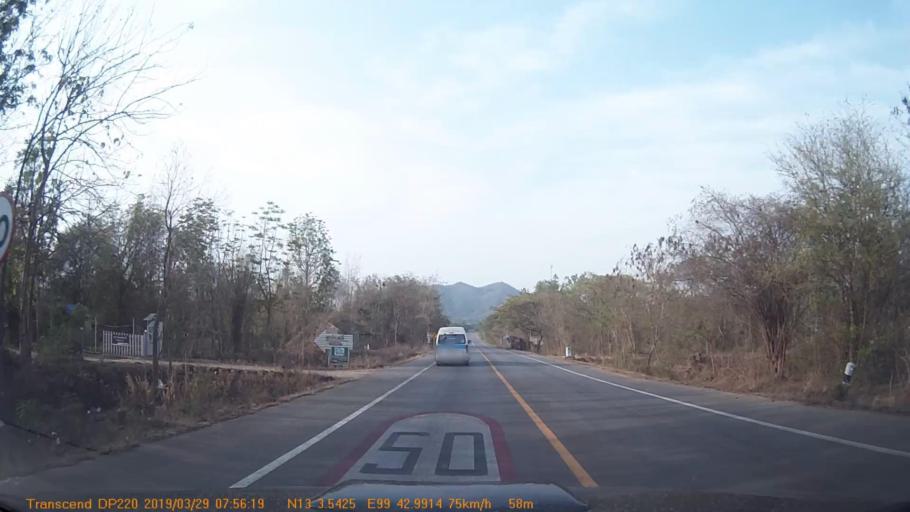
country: TH
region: Phetchaburi
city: Nong Ya Plong
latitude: 13.0586
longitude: 99.7165
